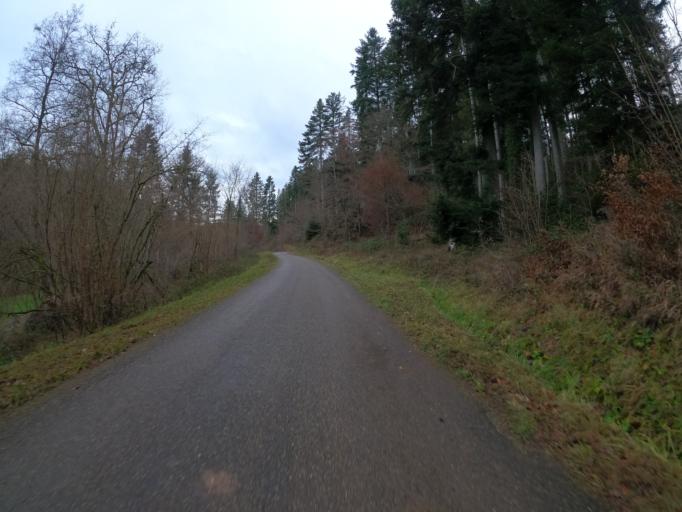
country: DE
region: Baden-Wuerttemberg
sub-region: Regierungsbezirk Stuttgart
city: Waschenbeuren
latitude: 48.7681
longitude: 9.7127
